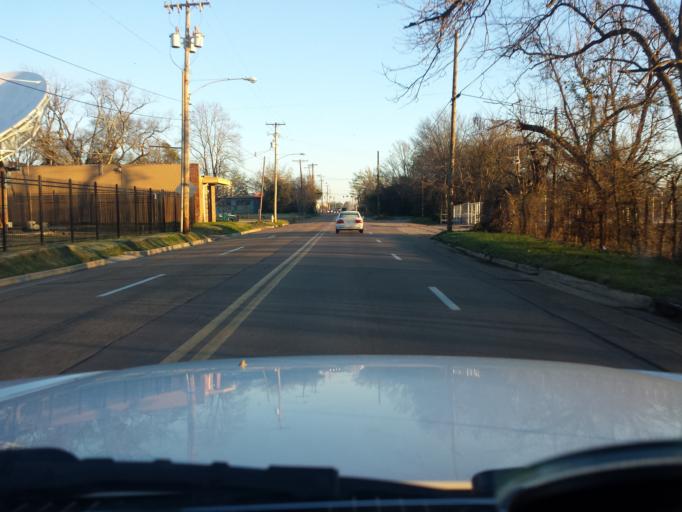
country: US
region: Mississippi
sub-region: Hinds County
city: Jackson
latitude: 32.2913
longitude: -90.1792
